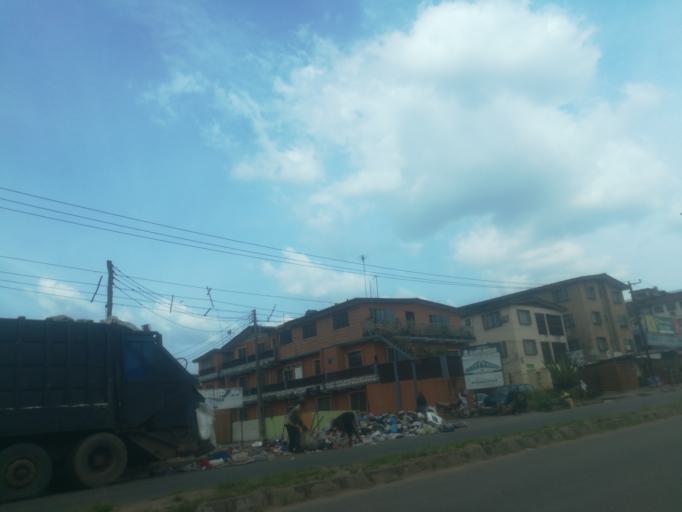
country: NG
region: Ogun
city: Abeokuta
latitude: 7.1359
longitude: 3.3285
